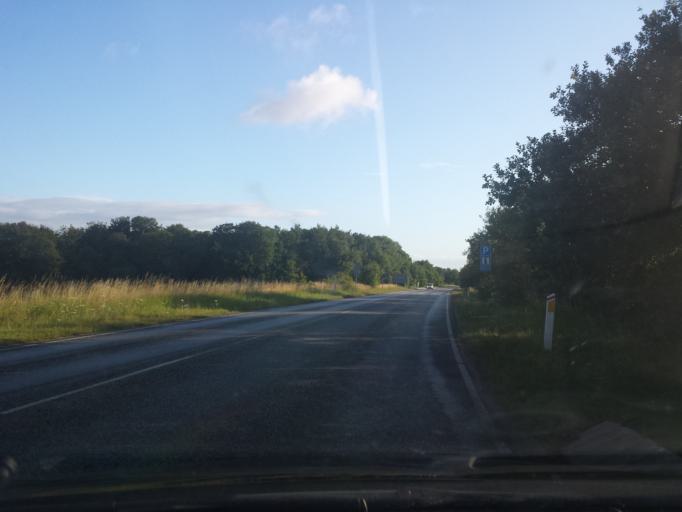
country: DK
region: South Denmark
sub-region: Sonderborg Kommune
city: Dybbol
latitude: 54.9121
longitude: 9.7074
